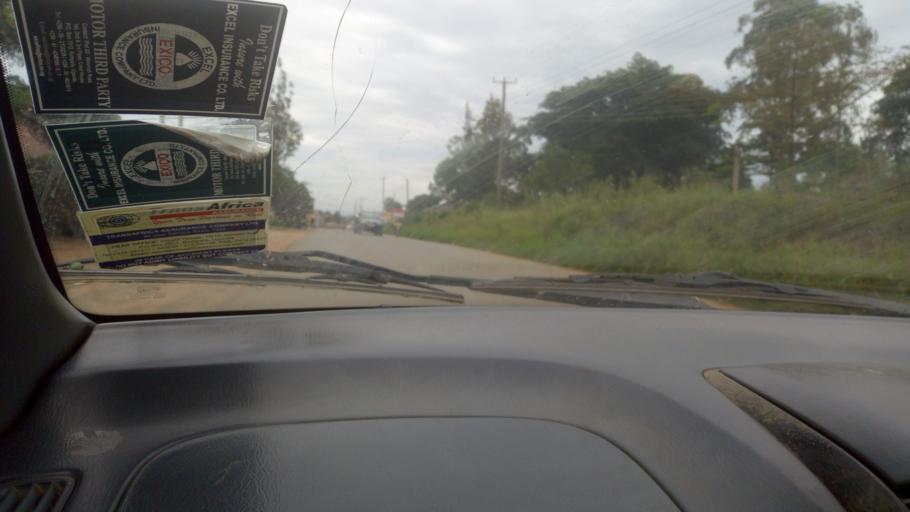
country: UG
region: Western Region
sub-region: Mbarara District
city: Mbarara
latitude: -0.6035
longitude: 30.6489
